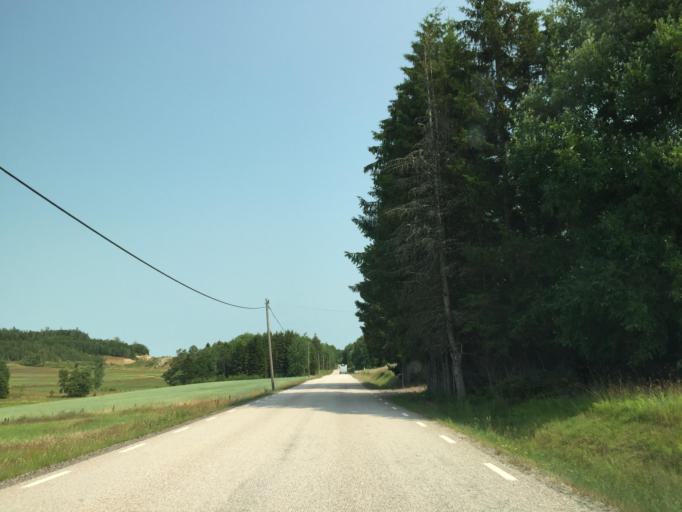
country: SE
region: Vaestra Goetaland
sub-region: Lilla Edets Kommun
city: Lilla Edet
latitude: 58.1454
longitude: 12.0197
